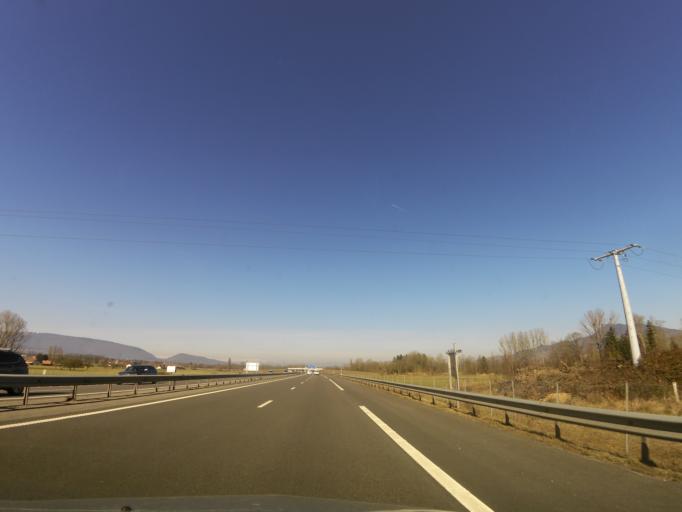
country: FR
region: Rhone-Alpes
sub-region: Departement de la Haute-Savoie
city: Arenthon
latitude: 46.1134
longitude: 6.3389
